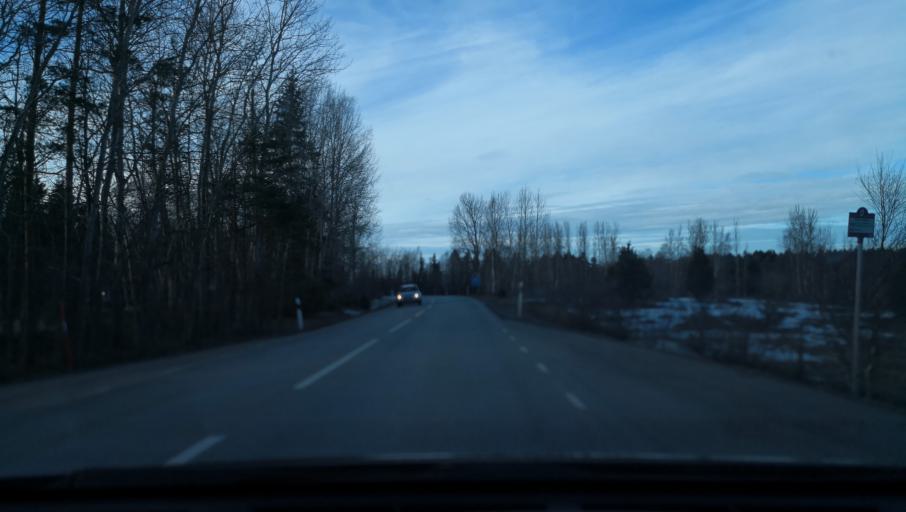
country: SE
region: Uppsala
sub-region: Osthammars Kommun
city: OEsthammar
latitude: 60.3085
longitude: 18.2701
